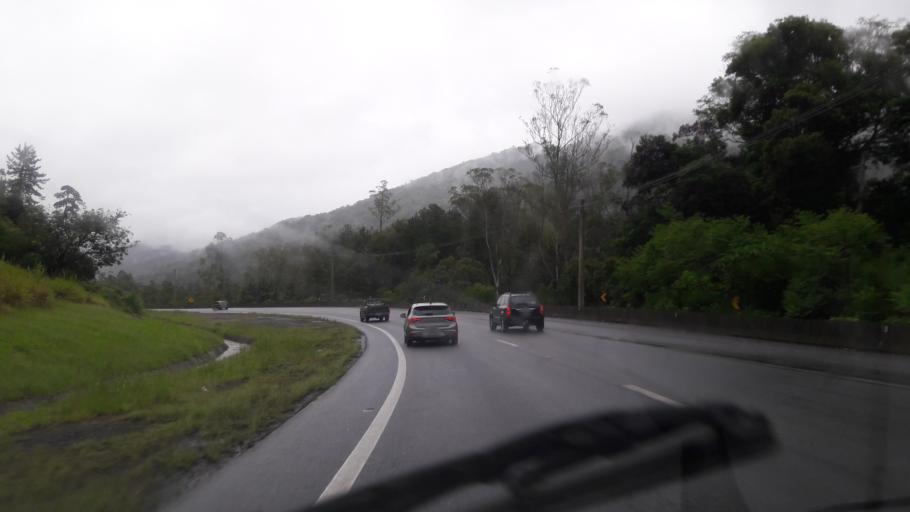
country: BR
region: Sao Paulo
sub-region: Juquitiba
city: Juquitiba
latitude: -24.0599
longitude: -47.2222
